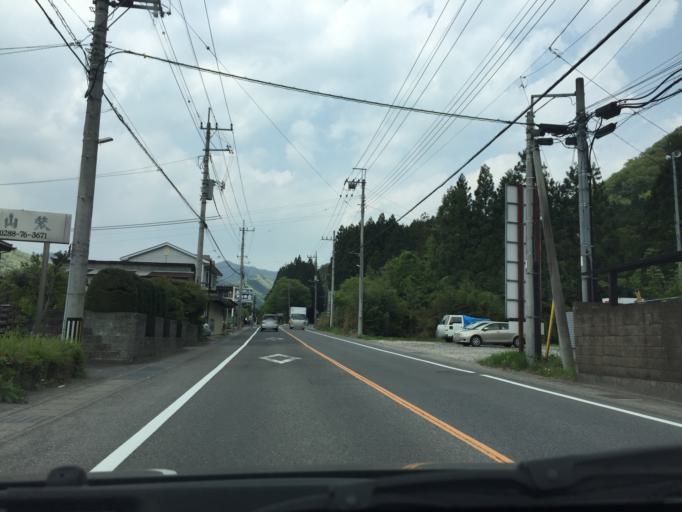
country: JP
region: Tochigi
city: Imaichi
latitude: 36.7908
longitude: 139.7054
